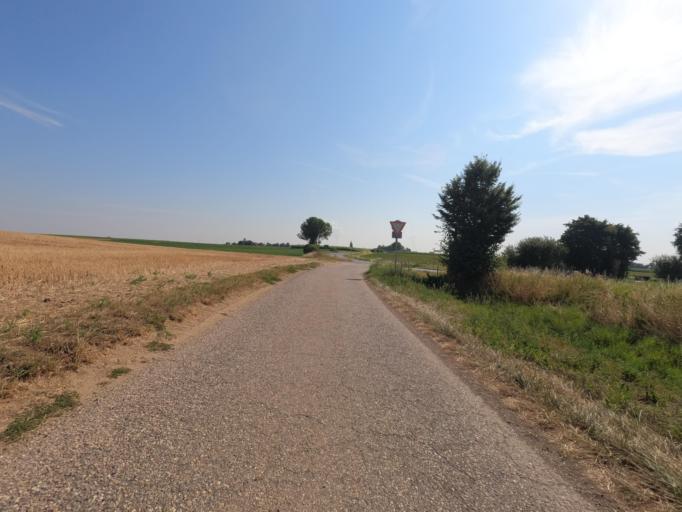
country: DE
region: North Rhine-Westphalia
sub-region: Regierungsbezirk Koln
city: Titz
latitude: 51.0030
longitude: 6.3548
